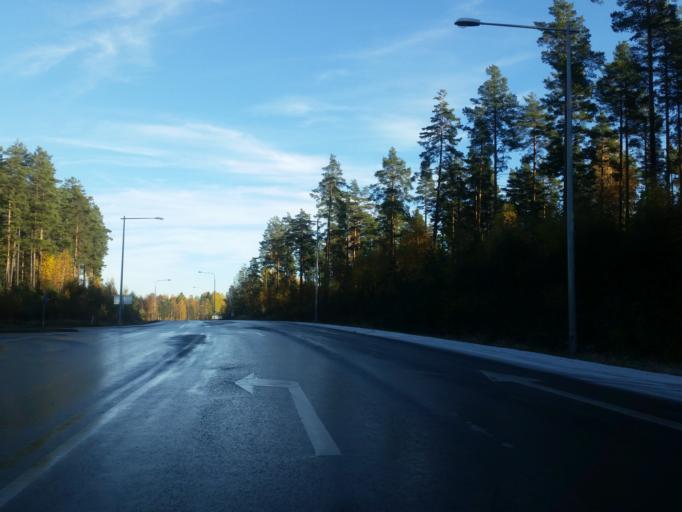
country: SE
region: Dalarna
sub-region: Faluns Kommun
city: Falun
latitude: 60.5747
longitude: 15.6082
